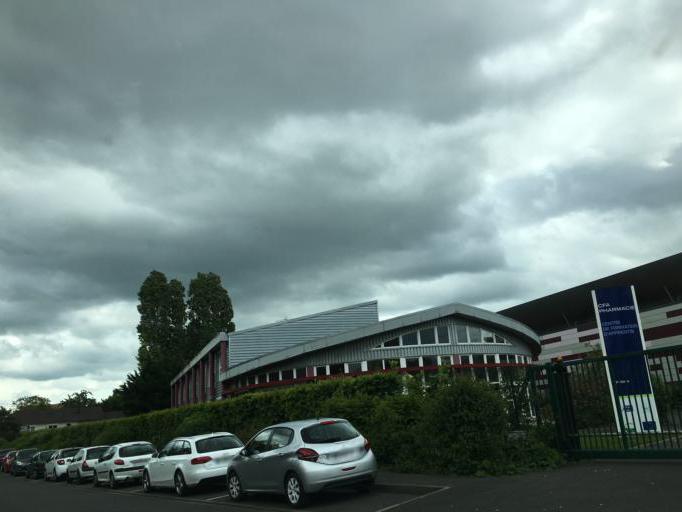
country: FR
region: Centre
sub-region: Departement du Loiret
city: Fleury-les-Aubrais
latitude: 47.9185
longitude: 1.9265
